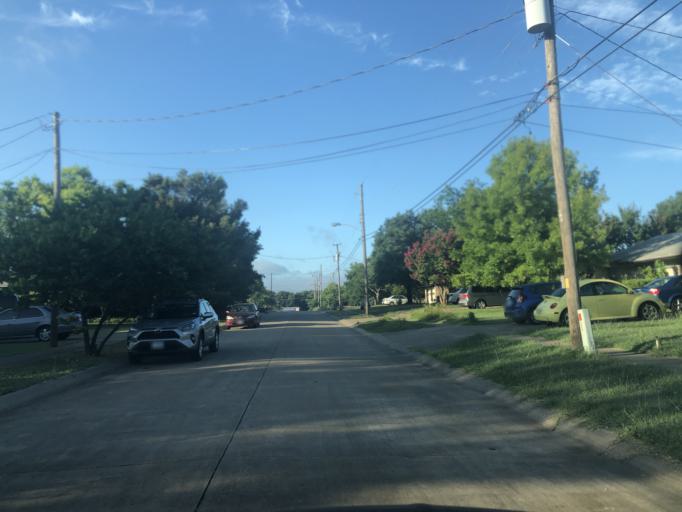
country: US
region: Texas
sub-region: Dallas County
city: Duncanville
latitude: 32.6682
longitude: -96.9523
